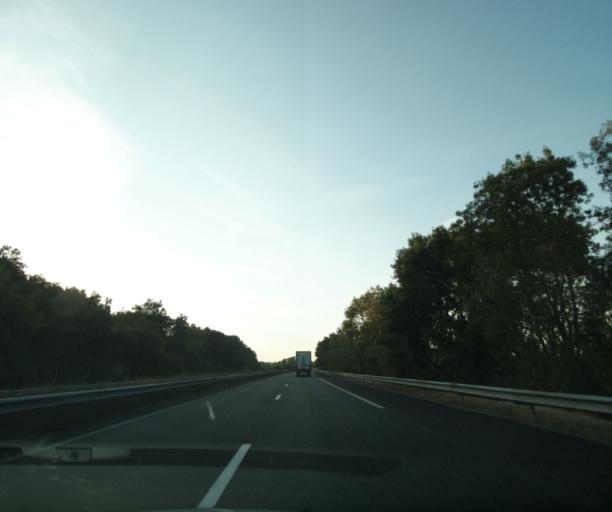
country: FR
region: Aquitaine
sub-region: Departement du Lot-et-Garonne
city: Layrac
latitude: 44.1307
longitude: 0.6830
